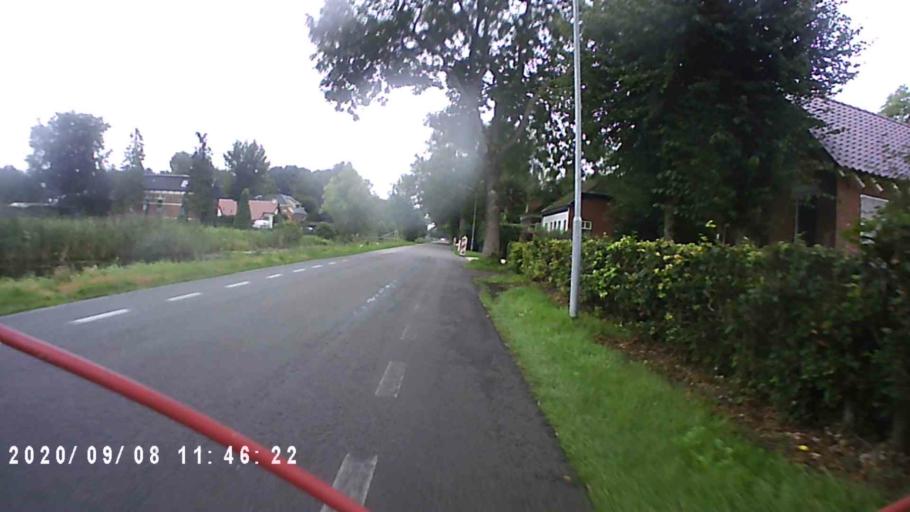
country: NL
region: Groningen
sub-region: Gemeente Hoogezand-Sappemeer
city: Sappemeer
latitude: 53.1452
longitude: 6.7983
